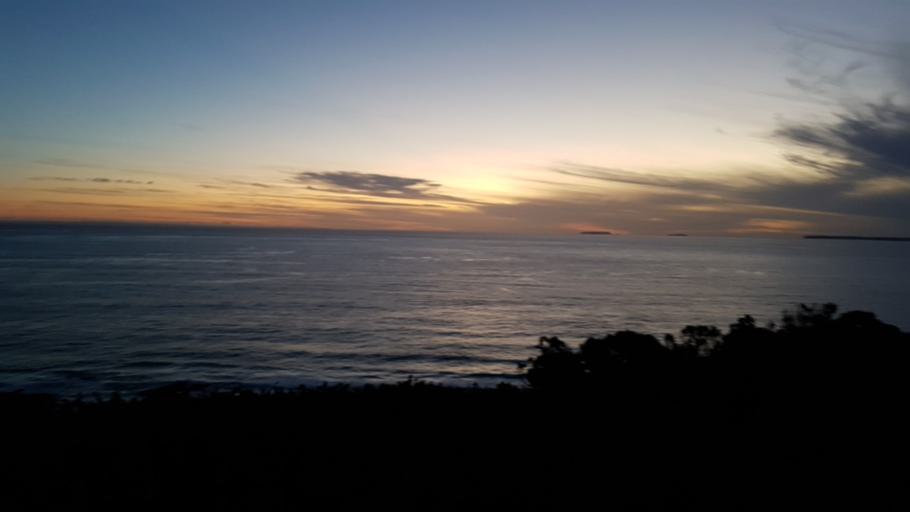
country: AU
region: South Australia
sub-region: Yorke Peninsula
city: Honiton
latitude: -35.2359
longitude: 137.1042
